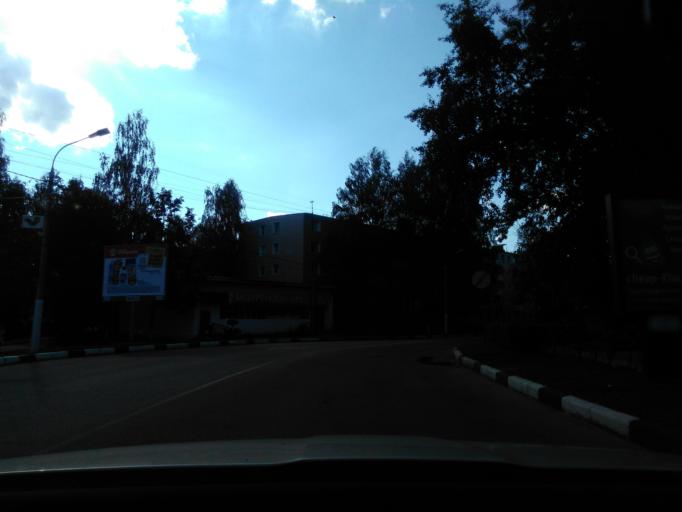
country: RU
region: Moskovskaya
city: Klin
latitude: 56.3199
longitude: 36.7240
